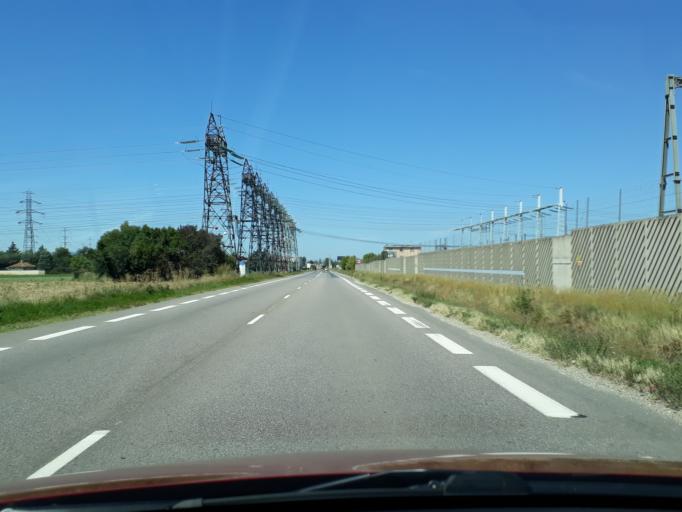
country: FR
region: Rhone-Alpes
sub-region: Departement du Rhone
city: Toussieu
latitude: 45.6726
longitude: 4.9761
